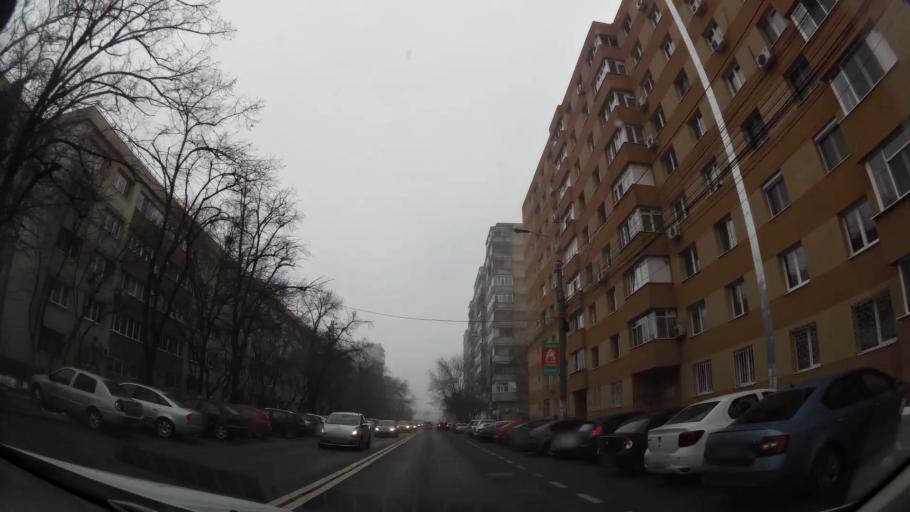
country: RO
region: Ilfov
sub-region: Comuna Chiajna
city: Rosu
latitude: 44.4546
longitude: 26.0445
